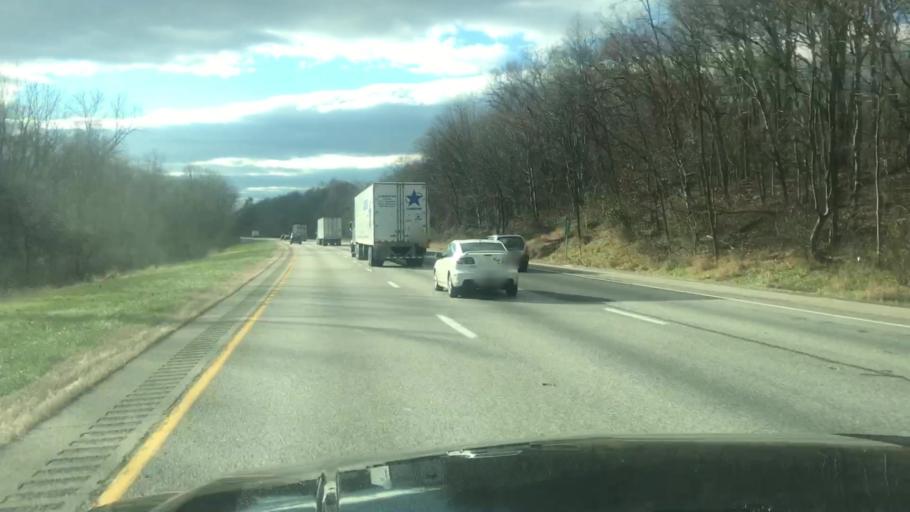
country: US
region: Pennsylvania
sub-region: Cumberland County
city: Enola
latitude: 40.3056
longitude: -76.9598
